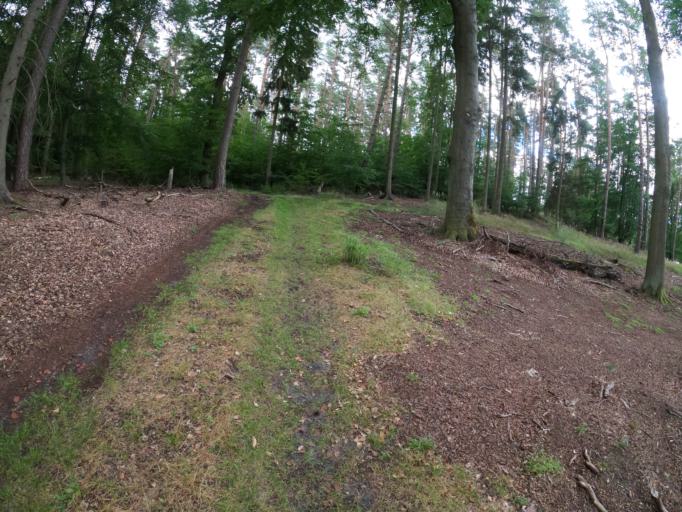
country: DE
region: Brandenburg
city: Angermunde
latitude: 53.0273
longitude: 13.9242
